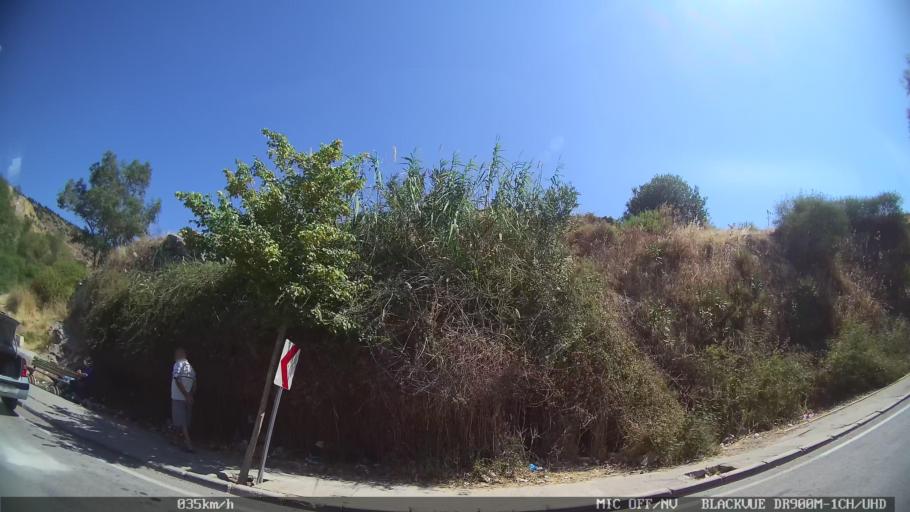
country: TR
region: Izmir
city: Karsiyaka
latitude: 38.5045
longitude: 27.0827
